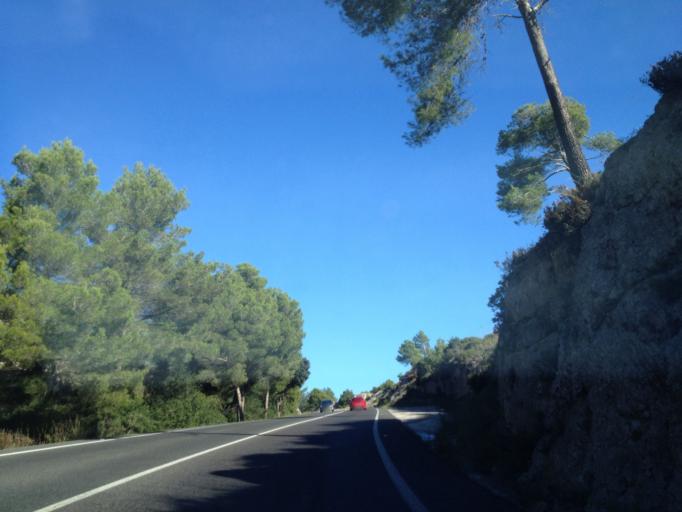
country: ES
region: Balearic Islands
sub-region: Illes Balears
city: Sant Llorenc des Cardassar
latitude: 39.6422
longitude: 3.3128
